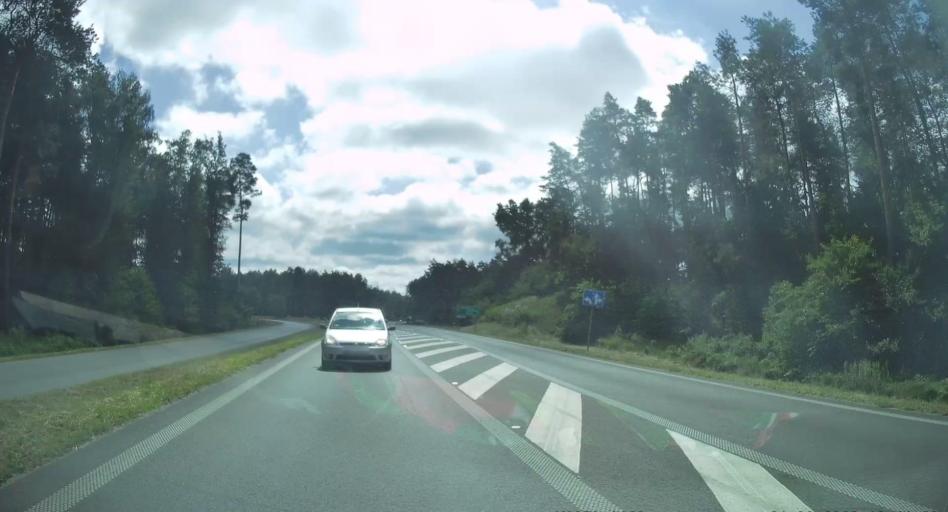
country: PL
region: Subcarpathian Voivodeship
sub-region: Powiat mielecki
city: Mielec
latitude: 50.3172
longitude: 21.5010
